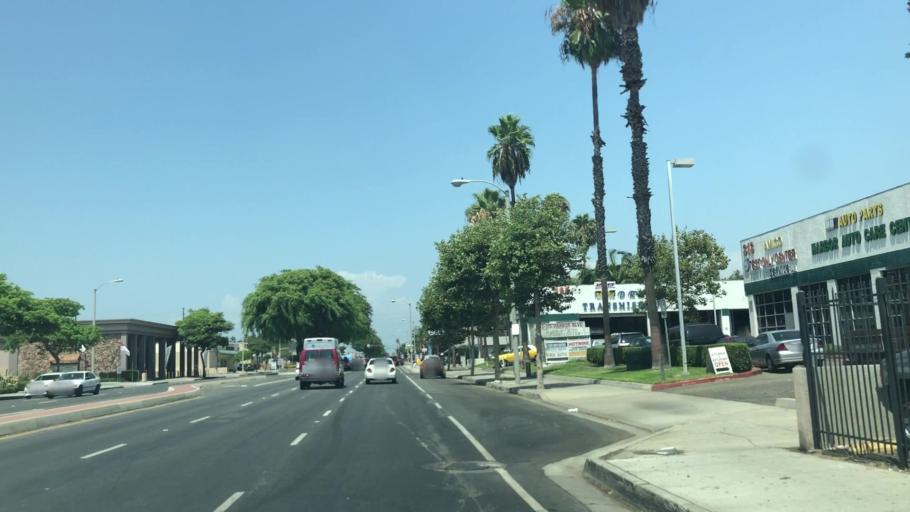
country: US
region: California
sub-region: Orange County
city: Garden Grove
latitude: 33.7424
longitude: -117.9200
